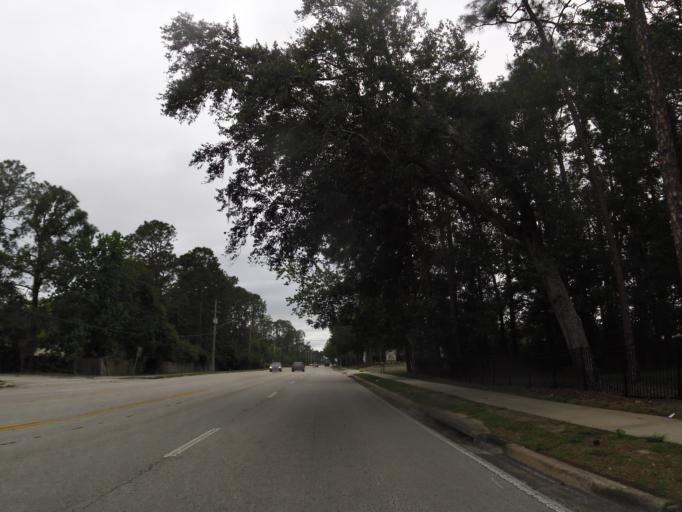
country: US
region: Florida
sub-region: Saint Johns County
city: Fruit Cove
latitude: 30.1919
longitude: -81.6092
